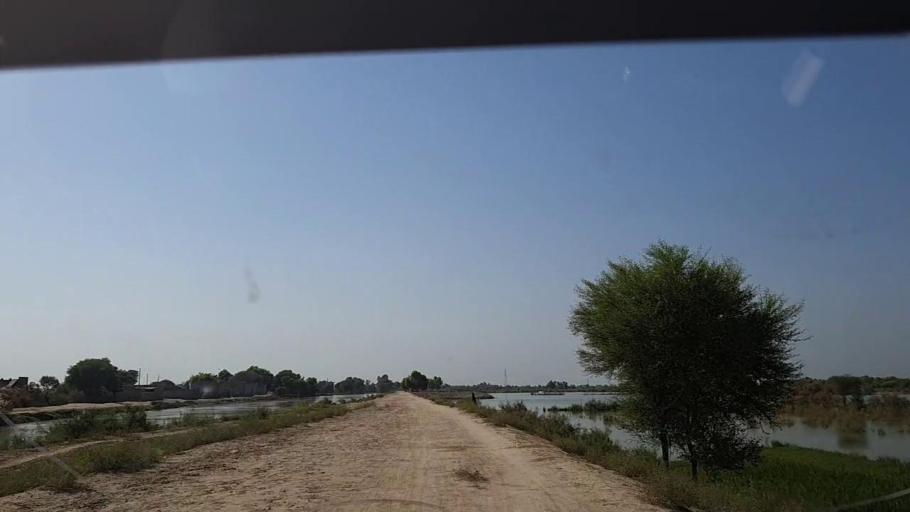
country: PK
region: Sindh
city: Ghauspur
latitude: 28.1783
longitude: 69.0913
